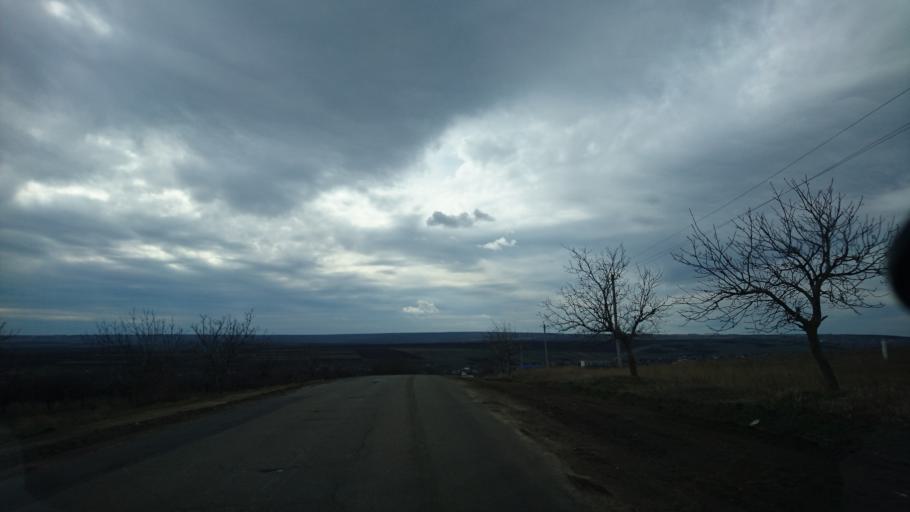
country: MD
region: Cantemir
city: Visniovca
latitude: 46.3292
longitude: 28.4644
